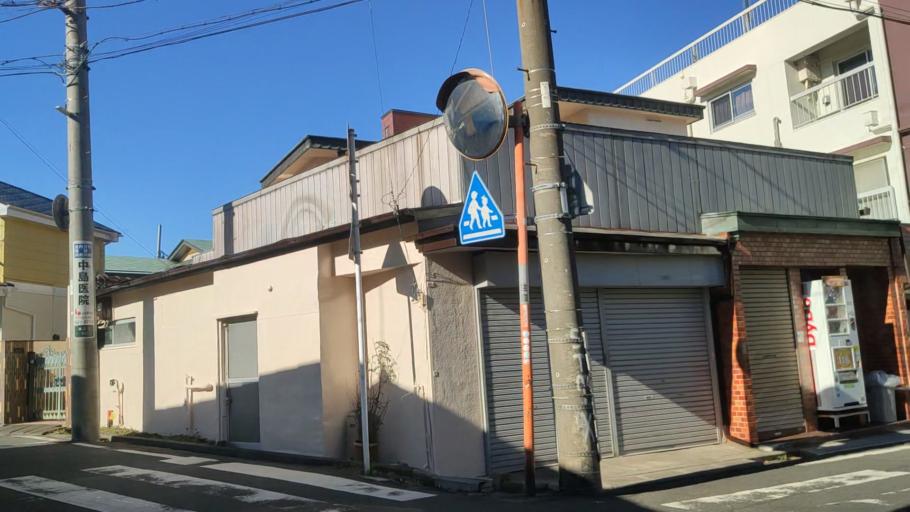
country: JP
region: Kanagawa
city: Yokohama
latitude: 35.4244
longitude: 139.6450
